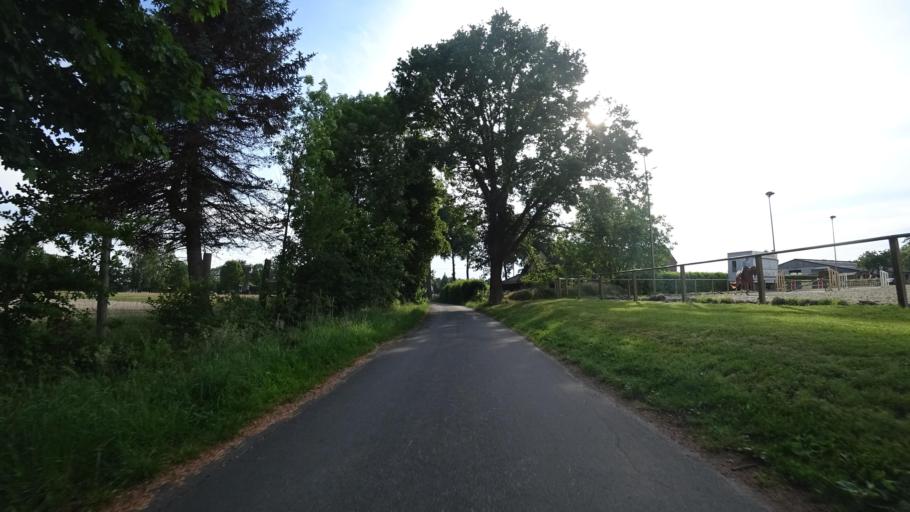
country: DE
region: North Rhine-Westphalia
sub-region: Regierungsbezirk Detmold
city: Verl
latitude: 51.9078
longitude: 8.4540
